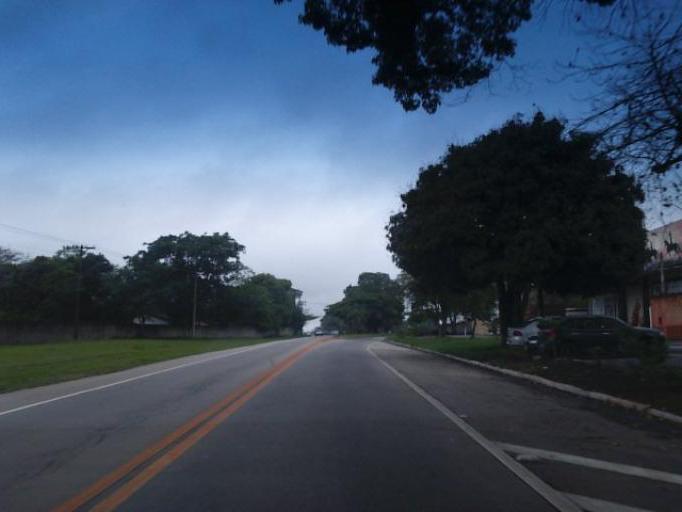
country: BR
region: Sao Paulo
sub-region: Sao Jose Dos Campos
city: Sao Jose dos Campos
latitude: -23.2270
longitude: -45.8729
